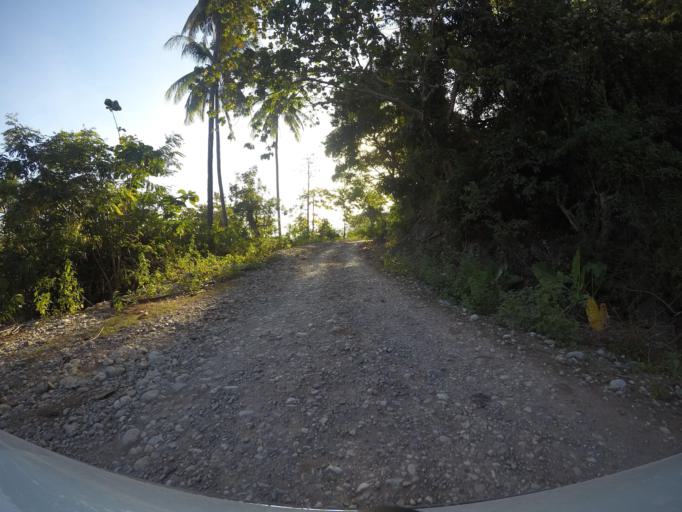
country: TL
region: Viqueque
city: Viqueque
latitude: -8.8014
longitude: 126.5642
